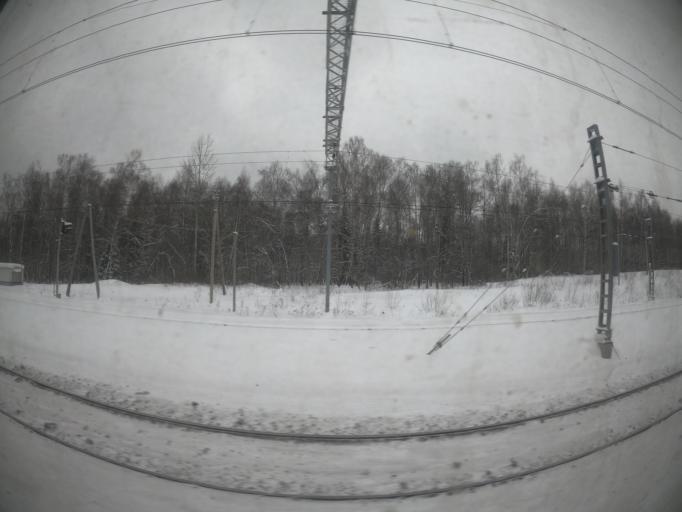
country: RU
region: Moskovskaya
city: Vostryakovo
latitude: 55.4317
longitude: 37.8486
